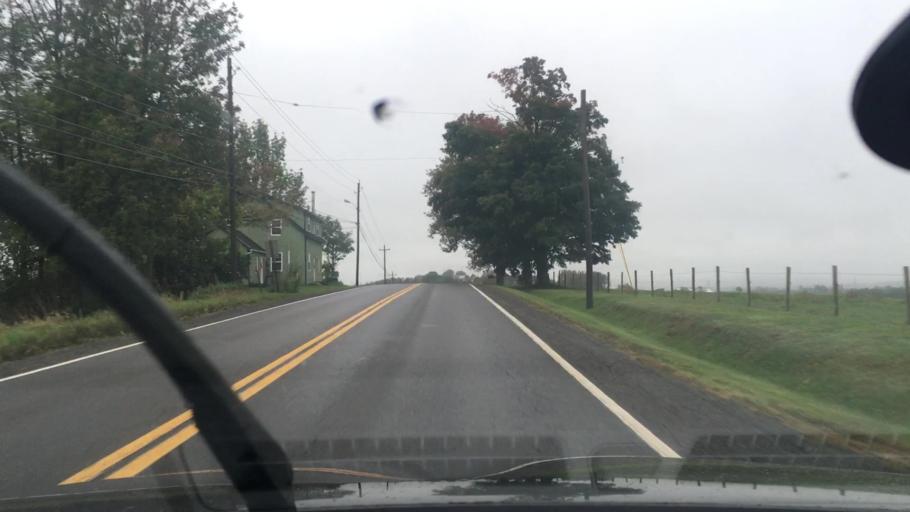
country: CA
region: Nova Scotia
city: Windsor
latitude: 44.9684
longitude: -64.1431
